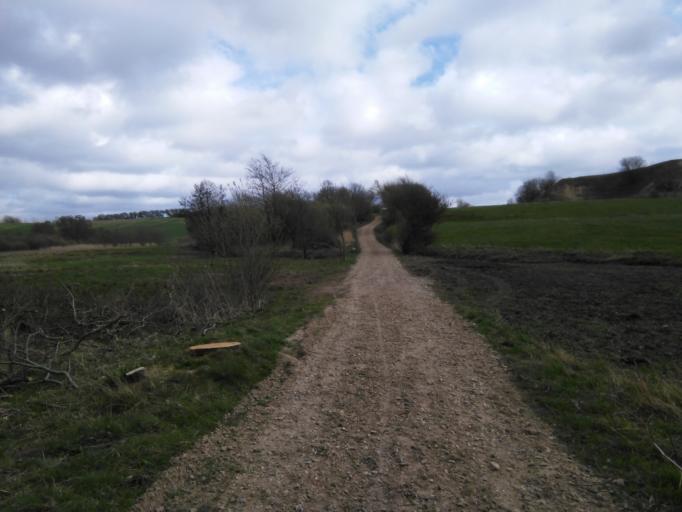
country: DK
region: Central Jutland
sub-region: Arhus Kommune
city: Beder
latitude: 56.0797
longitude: 10.1972
